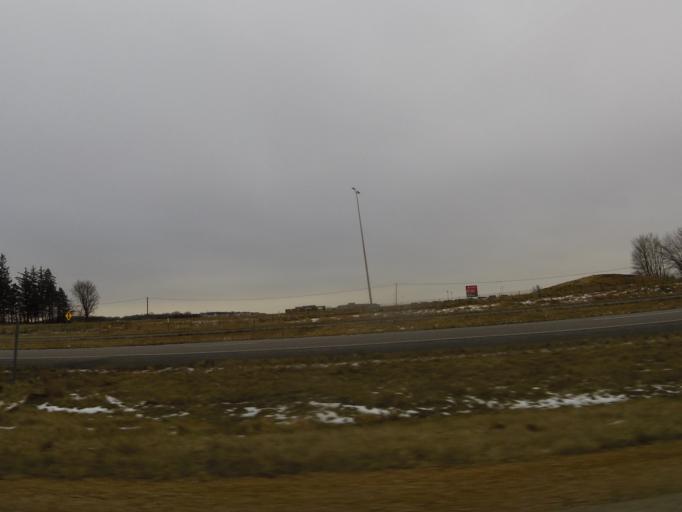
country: US
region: Minnesota
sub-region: Carver County
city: Carver
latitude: 44.7773
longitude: -93.6468
